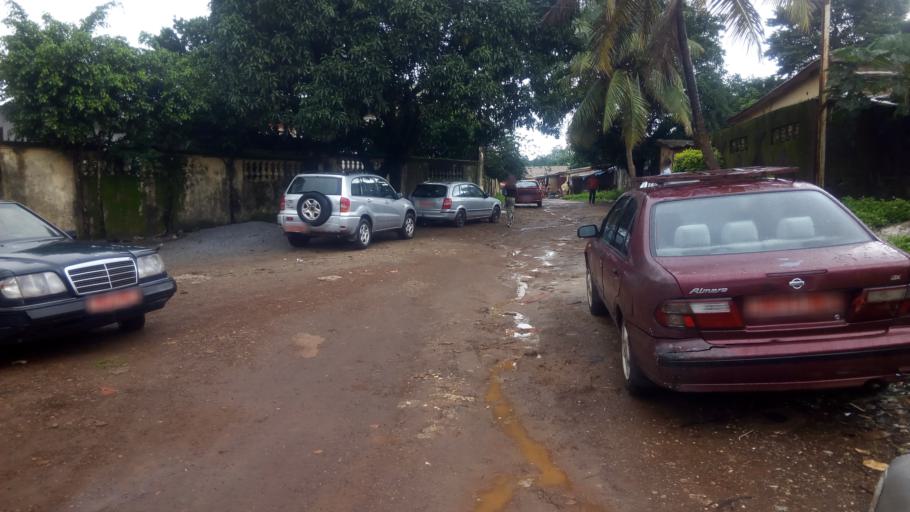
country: GN
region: Conakry
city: Conakry
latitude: 9.6387
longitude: -13.5607
